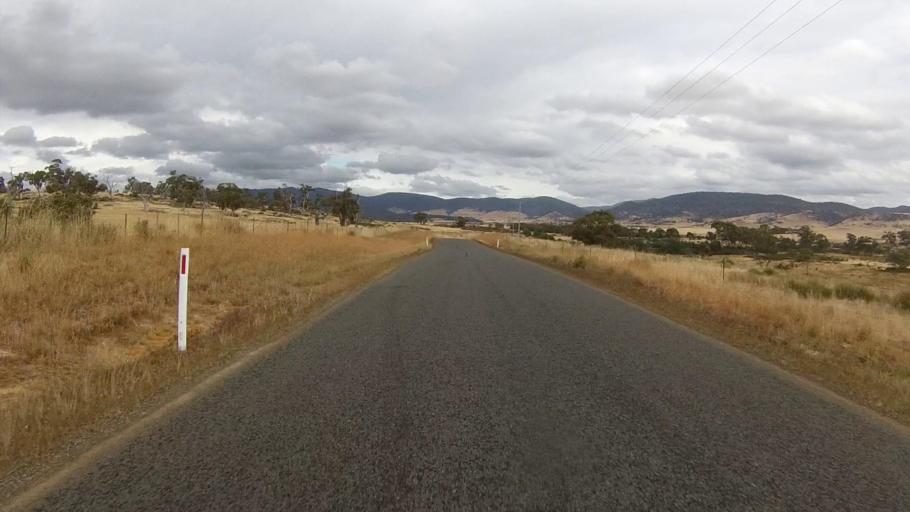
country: AU
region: Tasmania
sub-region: Northern Midlands
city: Evandale
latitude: -41.8073
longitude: 147.7532
